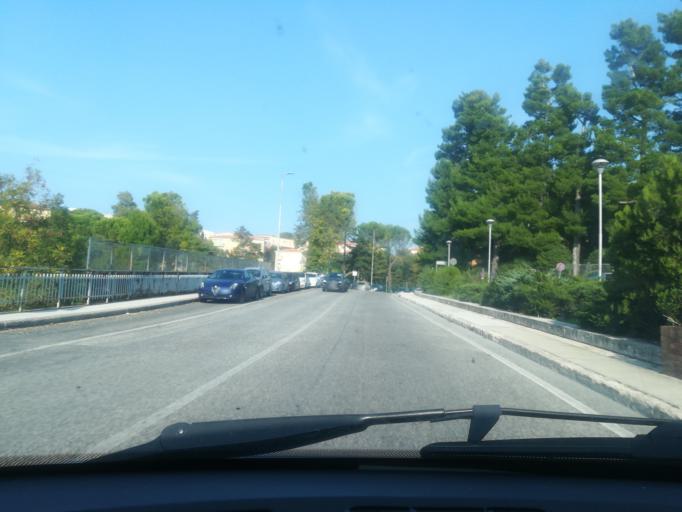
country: IT
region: The Marches
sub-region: Provincia di Macerata
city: Macerata
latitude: 43.2911
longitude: 13.4577
